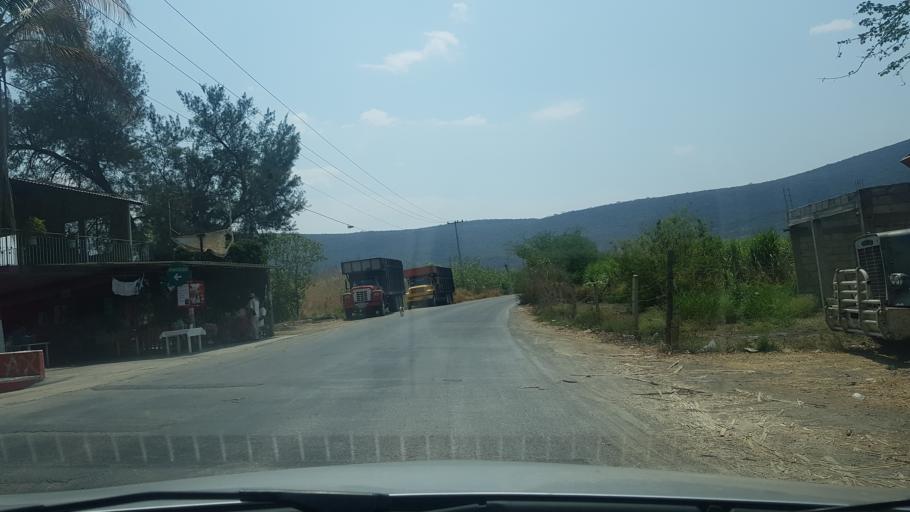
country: MX
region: Morelos
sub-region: Tlaltizapan de Zapata
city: Colonia Palo Prieto (Chipitongo)
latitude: 18.7329
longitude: -99.1159
